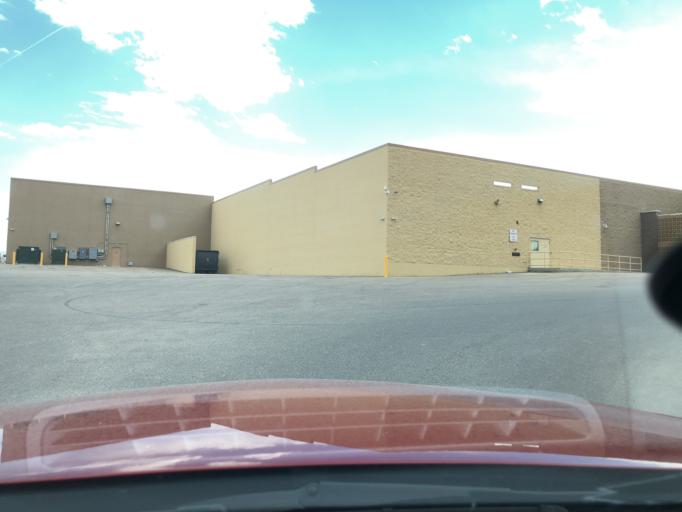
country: US
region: Colorado
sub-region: Jefferson County
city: Wheat Ridge
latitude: 39.7799
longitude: -105.0624
